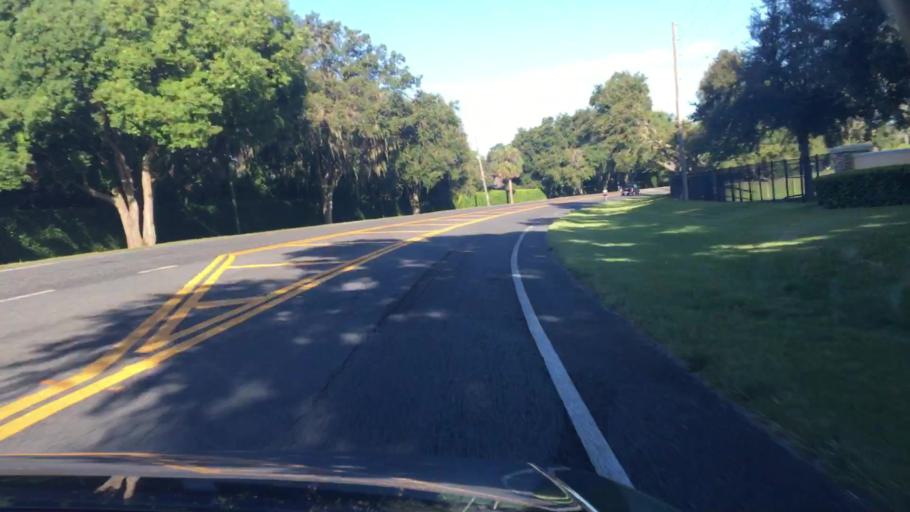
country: US
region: Florida
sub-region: Lake County
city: Eustis
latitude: 28.8513
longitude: -81.6419
